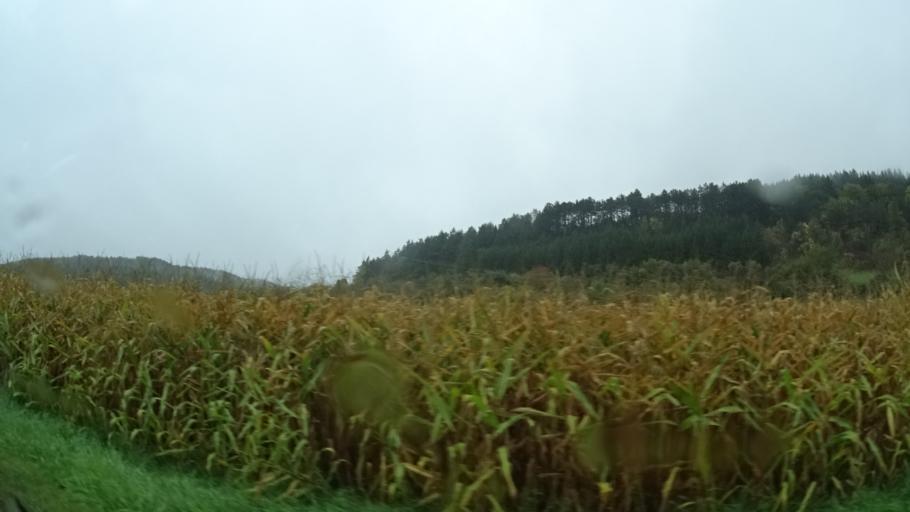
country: DE
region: Bavaria
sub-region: Upper Franconia
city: Marktrodach
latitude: 50.2706
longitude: 11.3585
